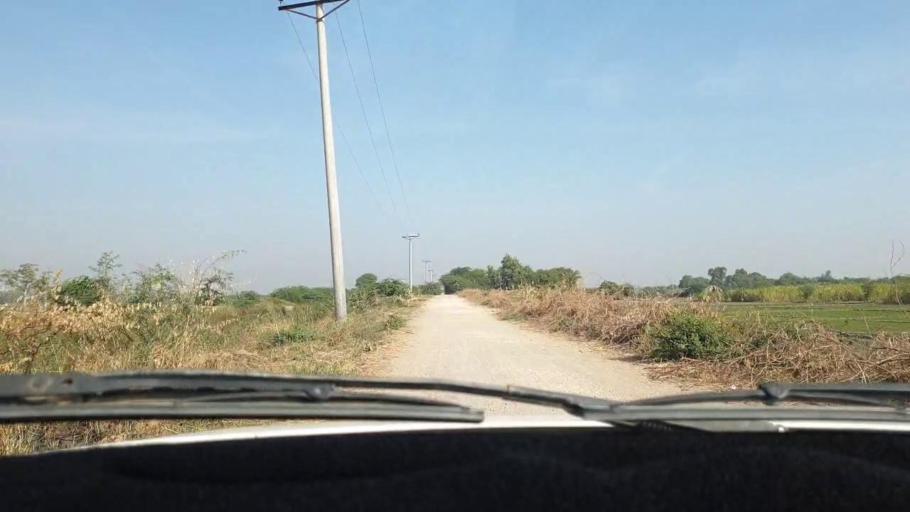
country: PK
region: Sindh
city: Bulri
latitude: 24.9678
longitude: 68.4558
